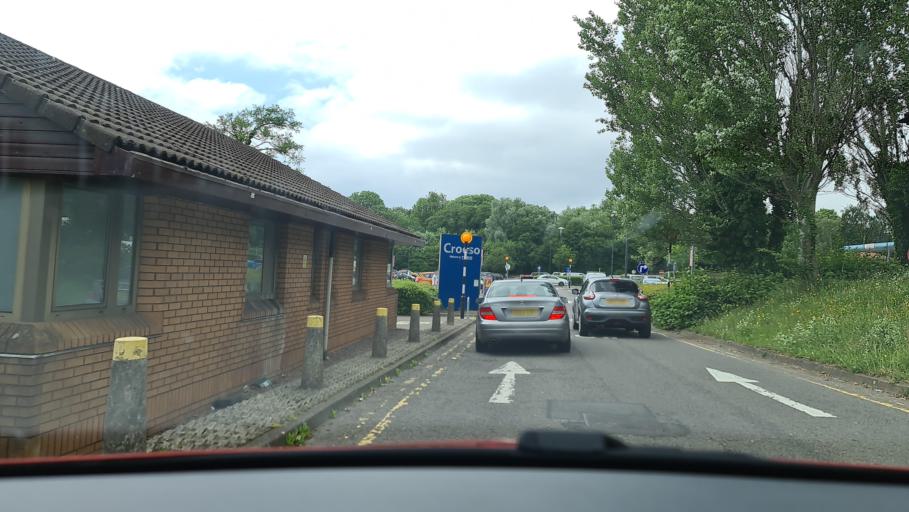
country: GB
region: Wales
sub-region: Newport
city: Marshfield
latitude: 51.5253
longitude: -3.1024
